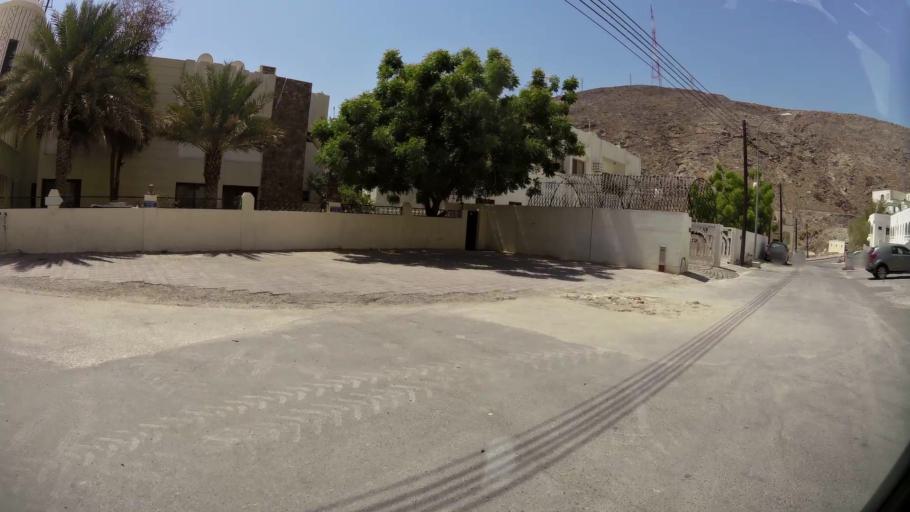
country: OM
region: Muhafazat Masqat
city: Muscat
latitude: 23.5969
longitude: 58.5321
